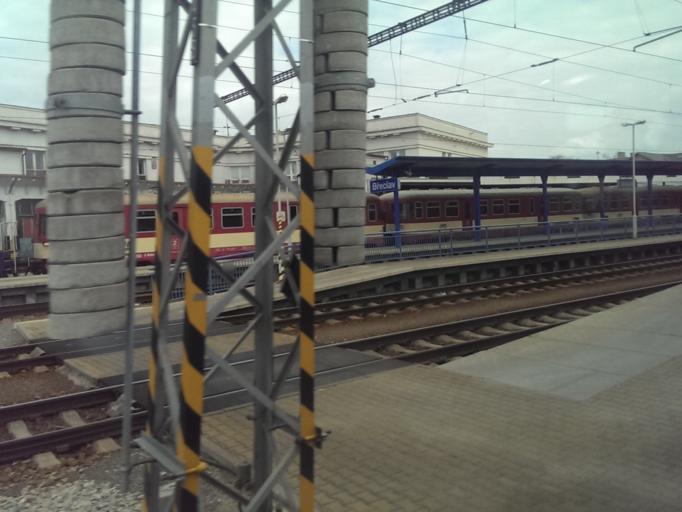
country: CZ
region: South Moravian
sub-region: Okres Breclav
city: Breclav
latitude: 48.7526
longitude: 16.8918
